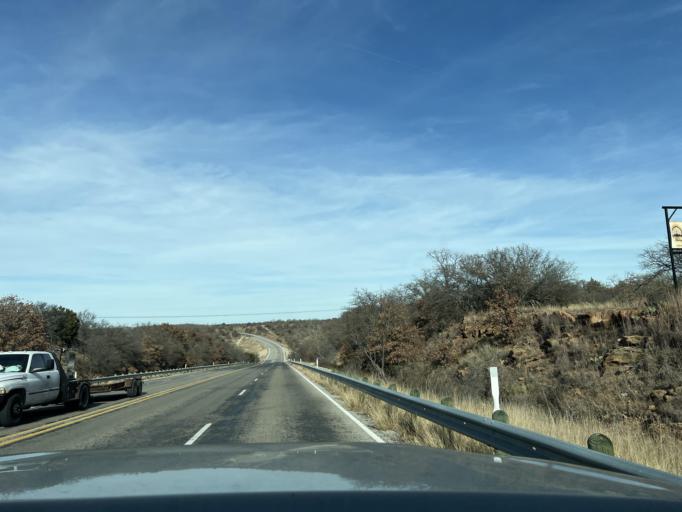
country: US
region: Texas
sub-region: Eastland County
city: Cisco
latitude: 32.4331
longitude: -98.9833
